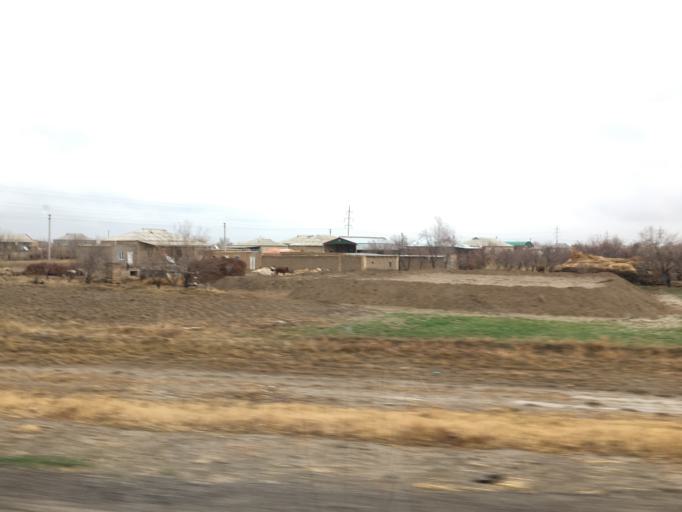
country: TM
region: Mary
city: Yoloeten
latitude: 37.3092
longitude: 62.3205
